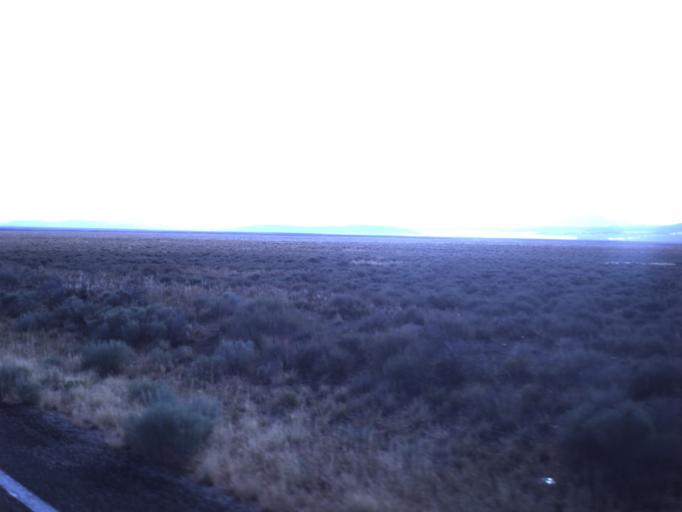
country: US
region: Utah
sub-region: Iron County
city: Enoch
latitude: 37.9292
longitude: -113.0298
